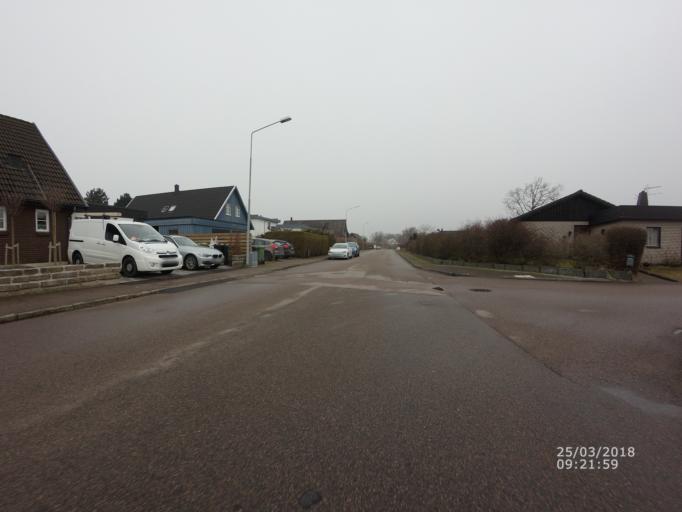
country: SE
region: Skane
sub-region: Hoganas Kommun
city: Hoganas
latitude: 56.1565
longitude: 12.5693
